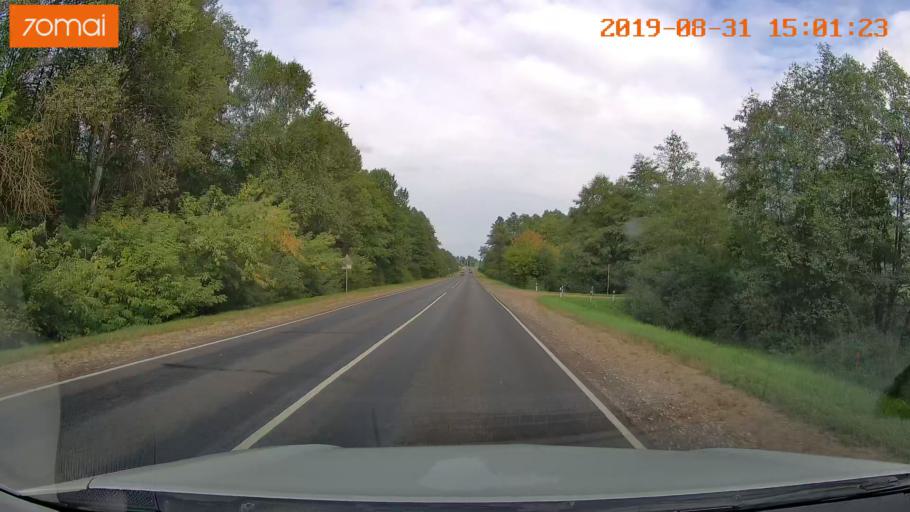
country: RU
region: Kaluga
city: Spas-Demensk
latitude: 54.3390
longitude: 34.0552
